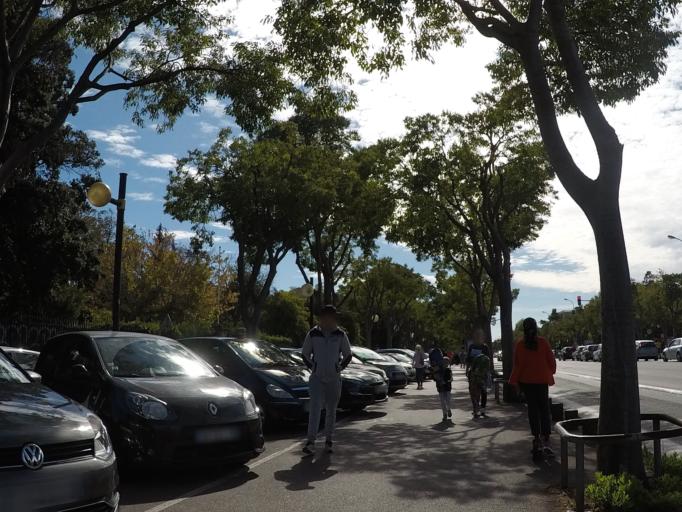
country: FR
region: Provence-Alpes-Cote d'Azur
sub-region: Departement des Bouches-du-Rhone
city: Marseille 08
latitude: 43.2657
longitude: 5.3809
